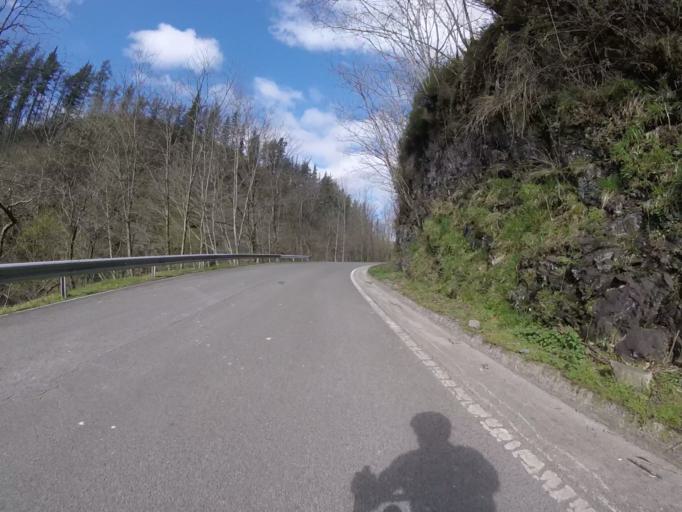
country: ES
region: Navarre
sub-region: Provincia de Navarra
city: Goizueta
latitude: 43.1608
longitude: -1.8508
